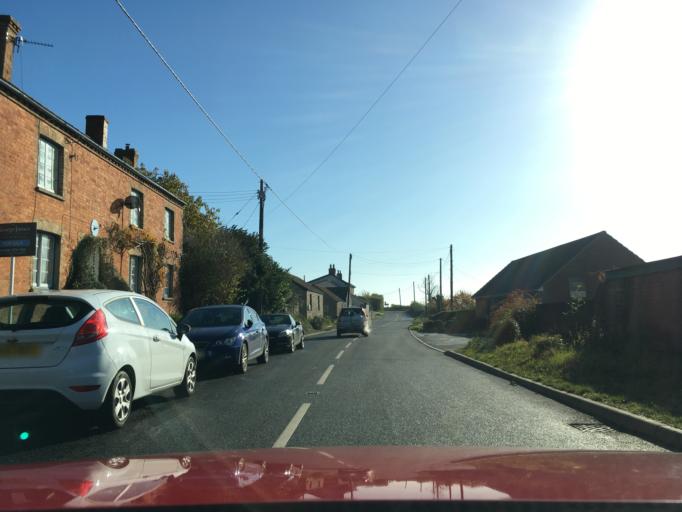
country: GB
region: England
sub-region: Somerset
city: Langport
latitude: 51.0573
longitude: -2.8535
